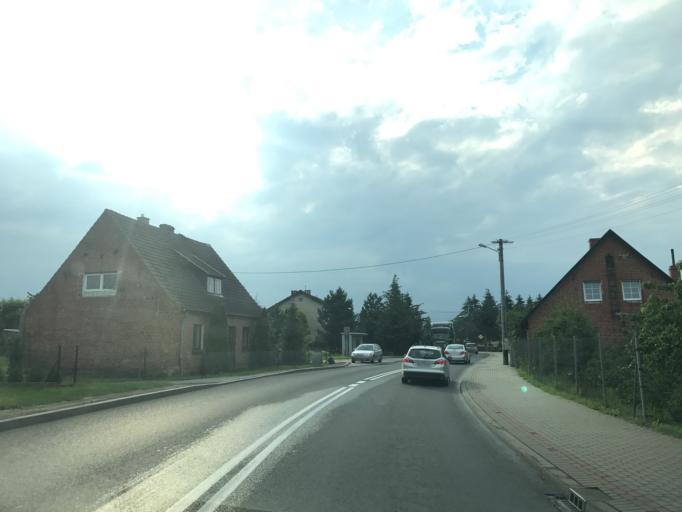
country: PL
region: Pomeranian Voivodeship
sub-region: Powiat czluchowski
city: Przechlewo
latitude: 53.7348
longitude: 17.1965
